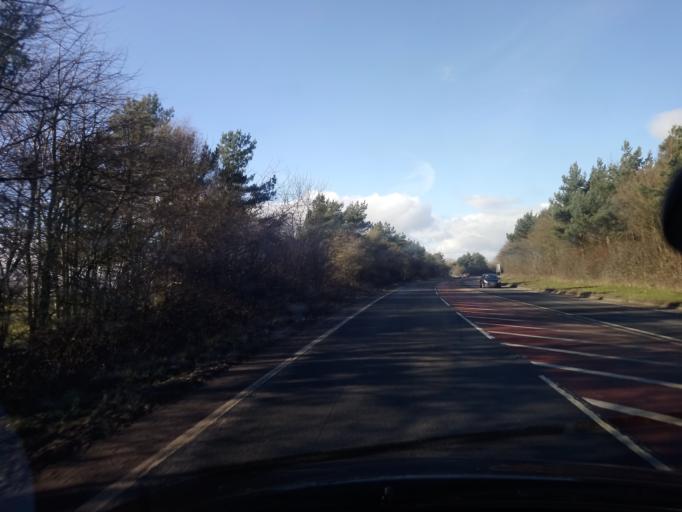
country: GB
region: England
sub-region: Shropshire
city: Whitchurch
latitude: 52.9570
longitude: -2.6916
